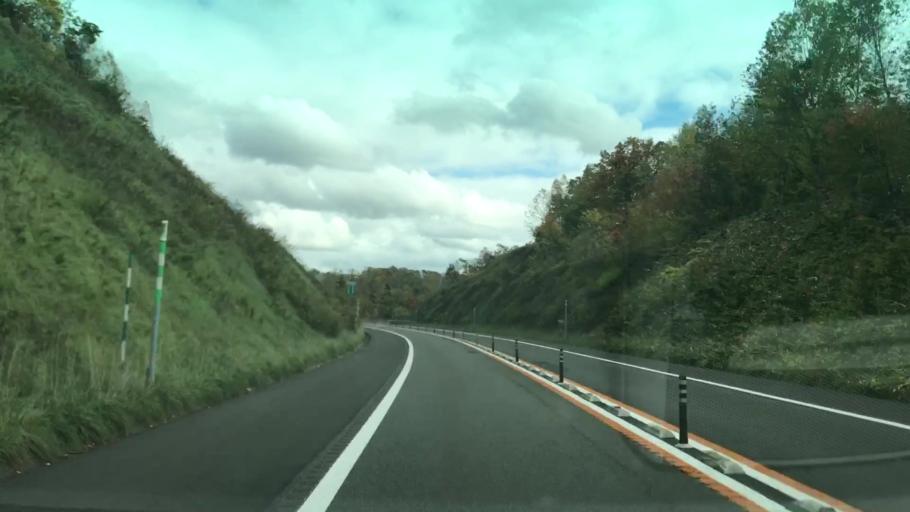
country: JP
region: Hokkaido
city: Chitose
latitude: 42.9165
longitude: 141.9622
